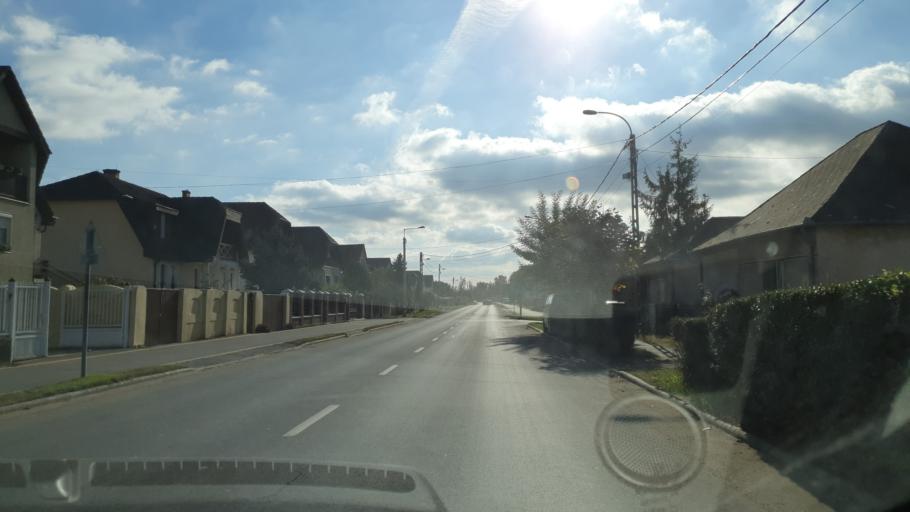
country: HU
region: Szabolcs-Szatmar-Bereg
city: Kisvarda
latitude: 48.2051
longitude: 22.0899
